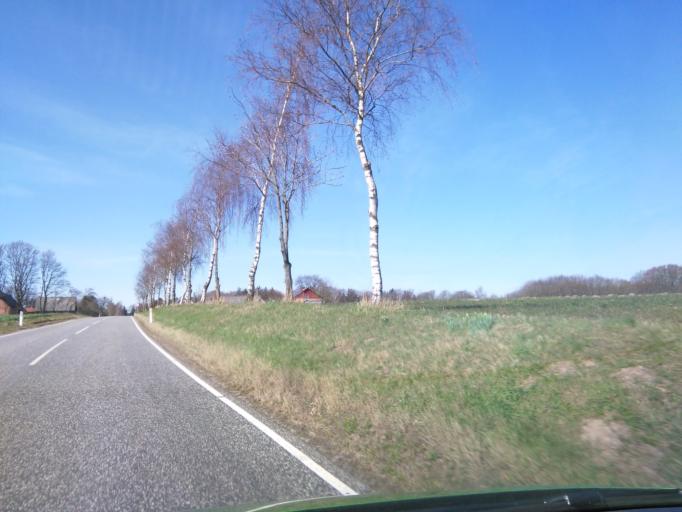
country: DK
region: Central Jutland
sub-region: Skanderborg Kommune
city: Ry
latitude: 56.0233
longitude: 9.7501
